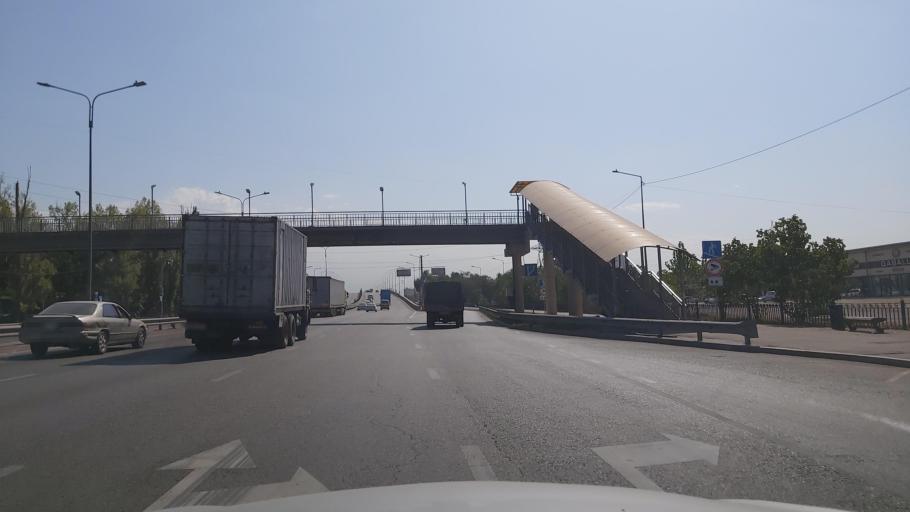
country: KZ
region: Almaty Qalasy
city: Almaty
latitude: 43.3073
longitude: 76.8976
